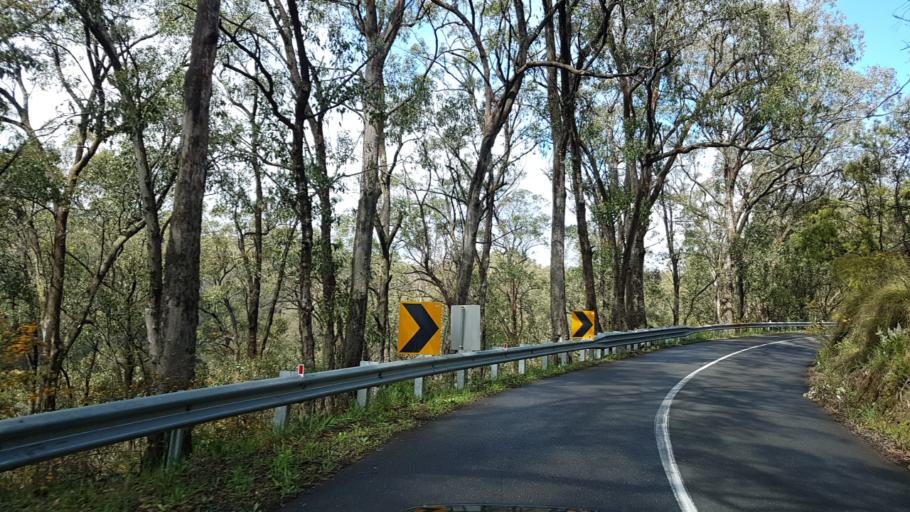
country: AU
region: South Australia
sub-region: Adelaide Hills
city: Adelaide Hills
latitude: -34.9135
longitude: 138.7571
